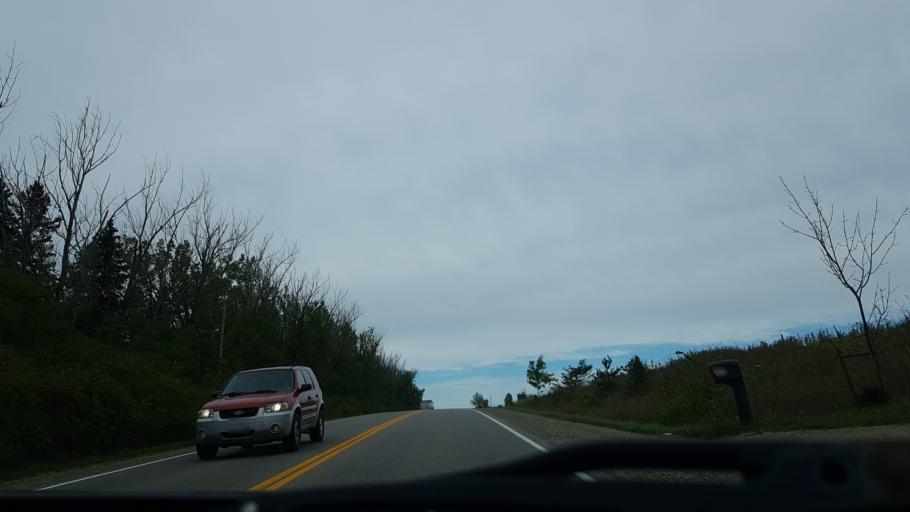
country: CA
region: Ontario
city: Shelburne
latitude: 44.0949
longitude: -80.0221
